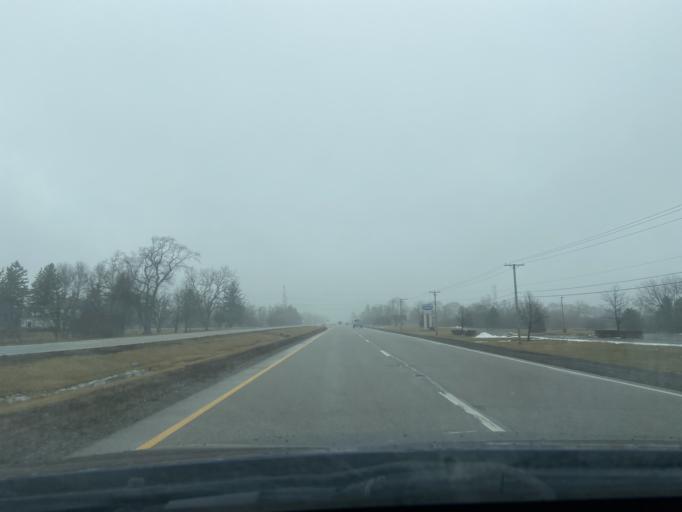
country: US
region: Illinois
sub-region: Lake County
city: Volo
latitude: 42.3018
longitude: -88.1647
